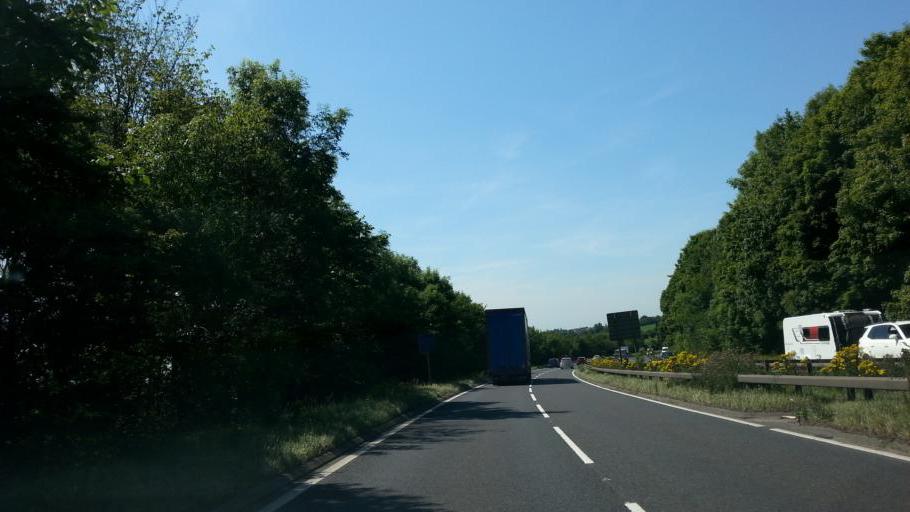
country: GB
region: England
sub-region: Derbyshire
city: Pinxton
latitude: 53.0958
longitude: -1.3281
